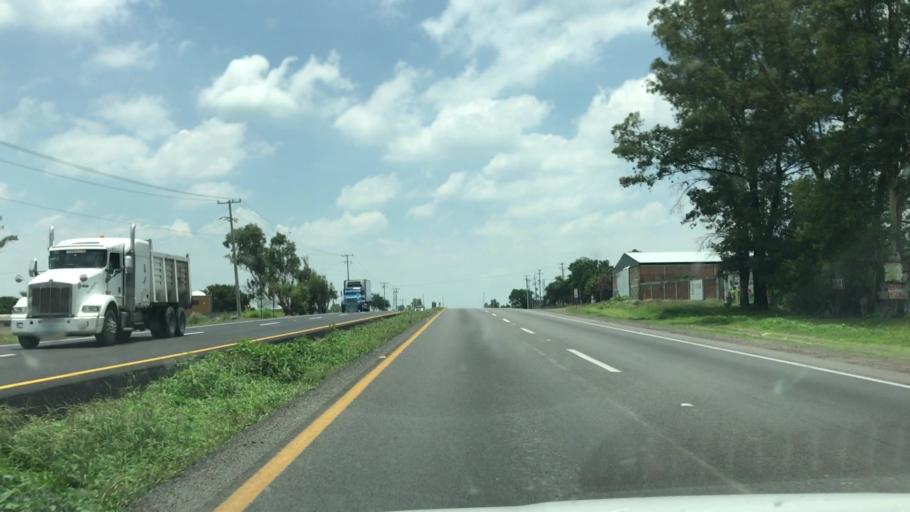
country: MX
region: Guanajuato
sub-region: Irapuato
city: San Ignacio de Rivera (Ojo de Agua)
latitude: 20.5416
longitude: -101.4562
